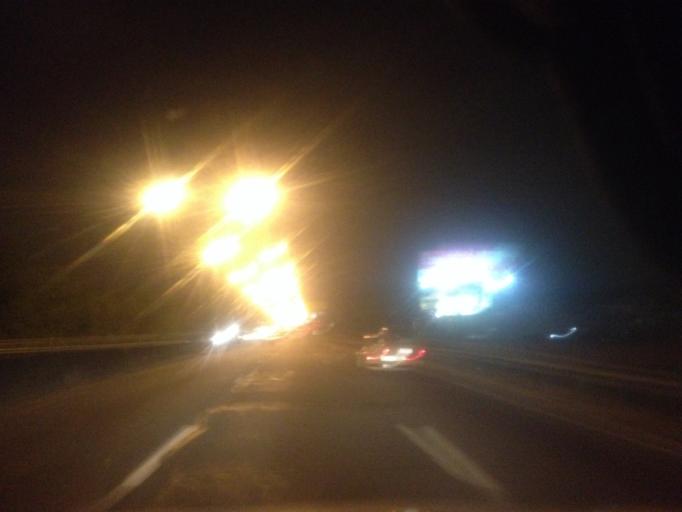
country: BR
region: Rio de Janeiro
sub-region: Duque De Caxias
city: Duque de Caxias
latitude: -22.8025
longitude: -43.3375
